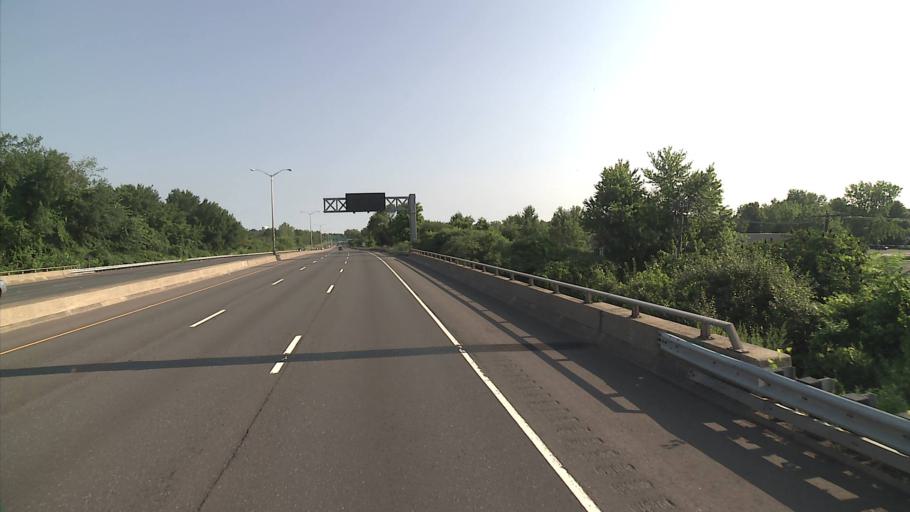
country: US
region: Connecticut
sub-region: Hartford County
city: Enfield
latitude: 41.9760
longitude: -72.5871
